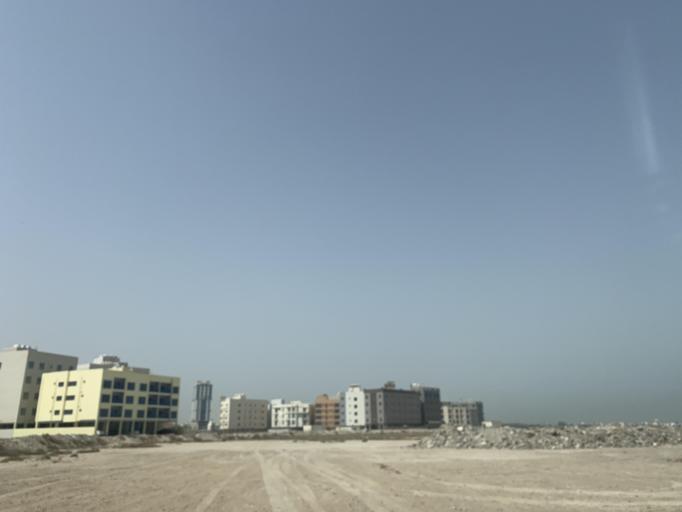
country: BH
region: Manama
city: Jidd Hafs
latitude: 26.2424
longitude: 50.5297
